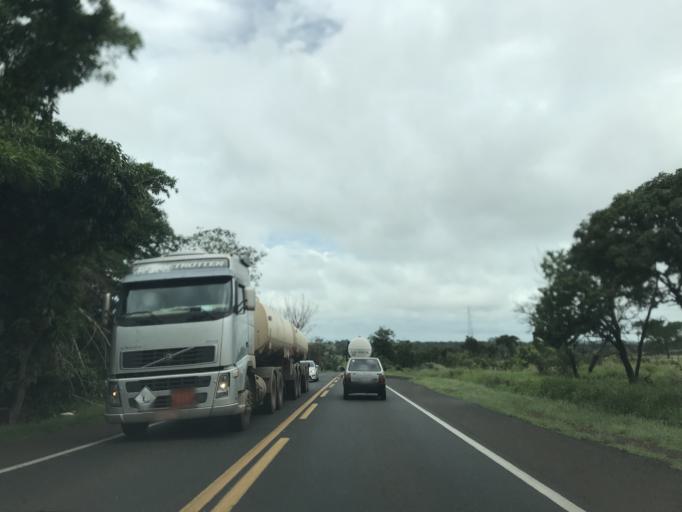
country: BR
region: Minas Gerais
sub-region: Frutal
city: Frutal
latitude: -19.8048
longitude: -48.9676
